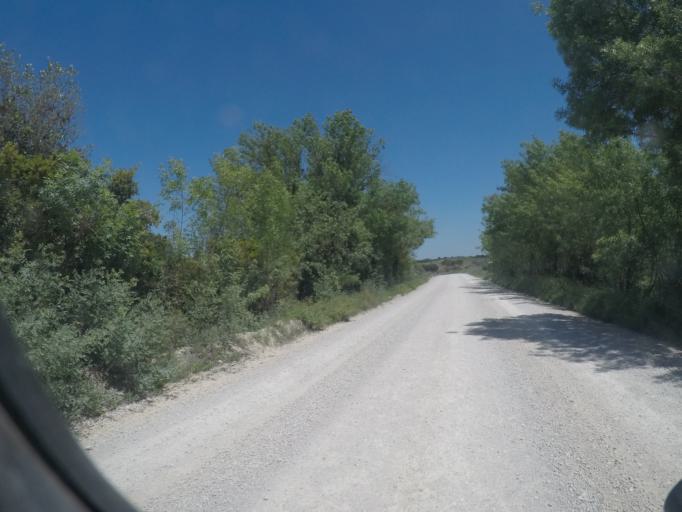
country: PT
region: Setubal
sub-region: Sesimbra
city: Sesimbra
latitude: 38.4678
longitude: -9.0458
